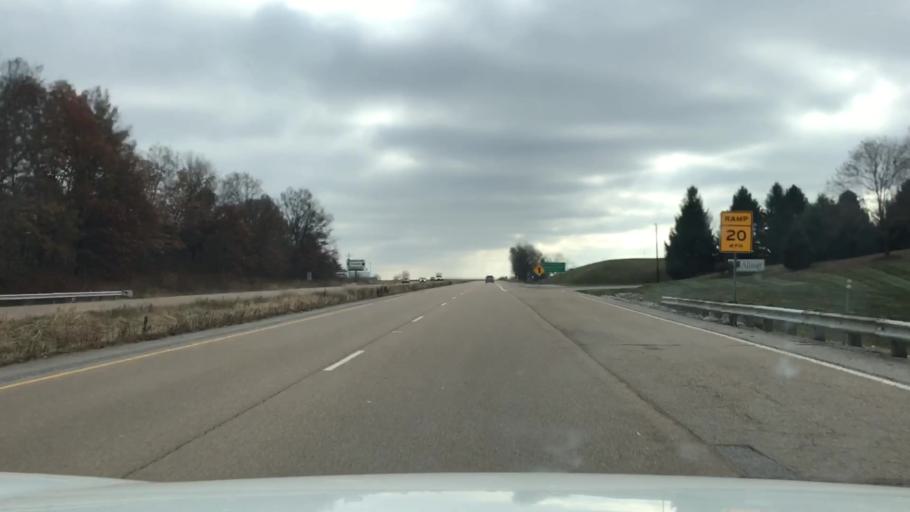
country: US
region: Illinois
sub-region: Saint Clair County
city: Swansea
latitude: 38.5306
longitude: -90.0432
